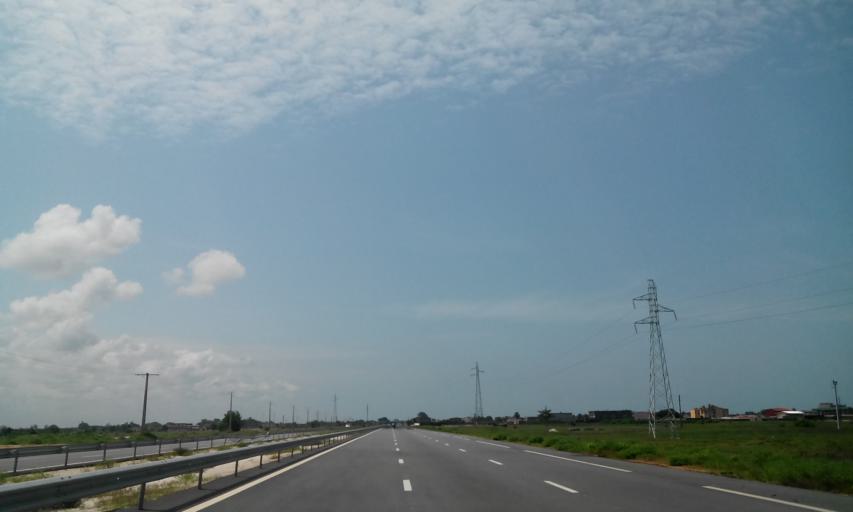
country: CI
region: Sud-Comoe
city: Grand-Bassam
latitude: 5.2273
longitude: -3.7423
